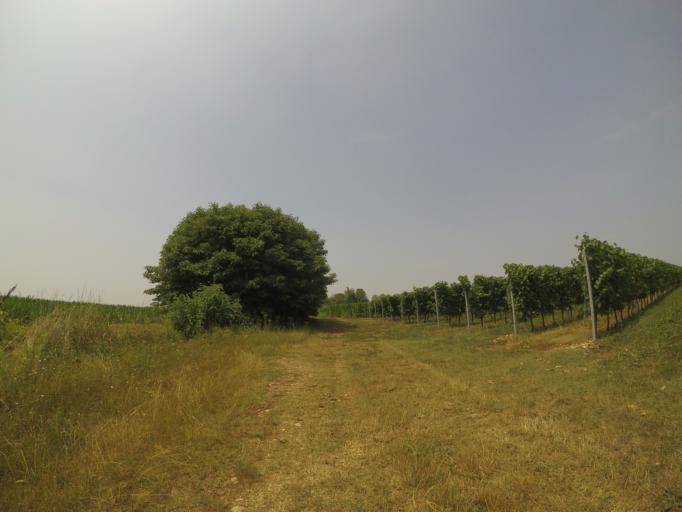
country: IT
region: Friuli Venezia Giulia
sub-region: Provincia di Udine
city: Bertiolo
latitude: 45.9550
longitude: 13.0440
